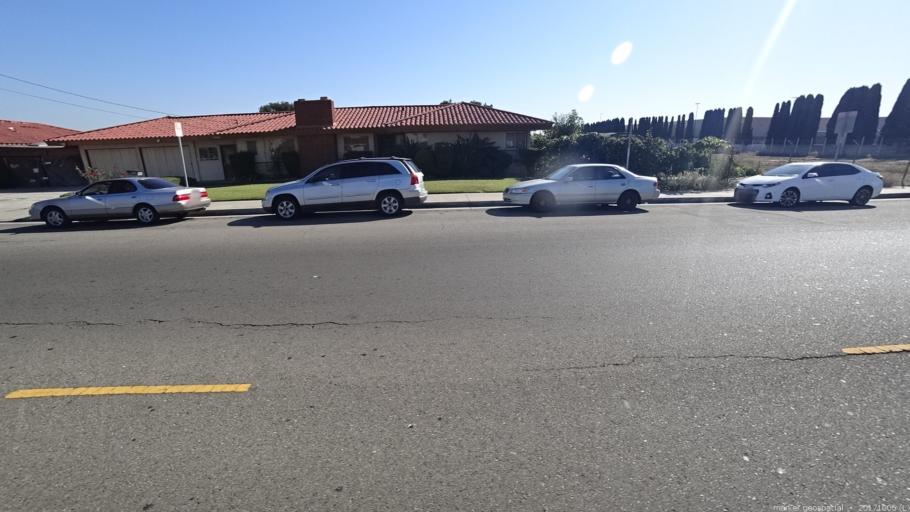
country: US
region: California
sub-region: Orange County
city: Stanton
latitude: 33.7812
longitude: -117.9889
